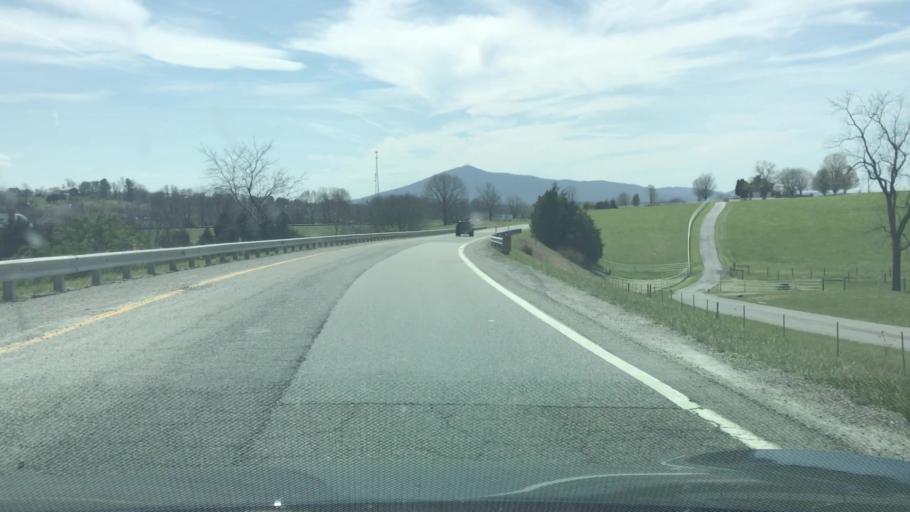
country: US
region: Virginia
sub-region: Pulaski County
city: Dublin
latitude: 37.0807
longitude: -80.6916
